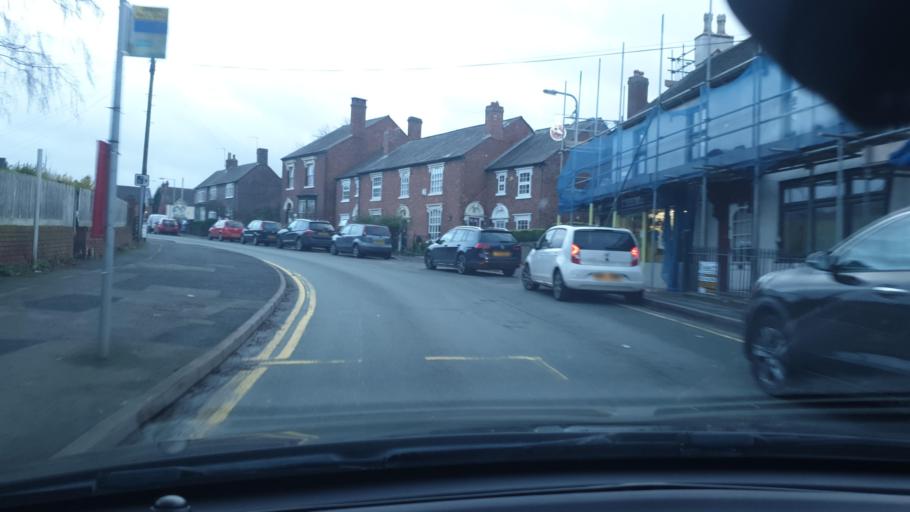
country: GB
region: England
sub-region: Staffordshire
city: Great Wyrley
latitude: 52.6614
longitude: -2.0316
